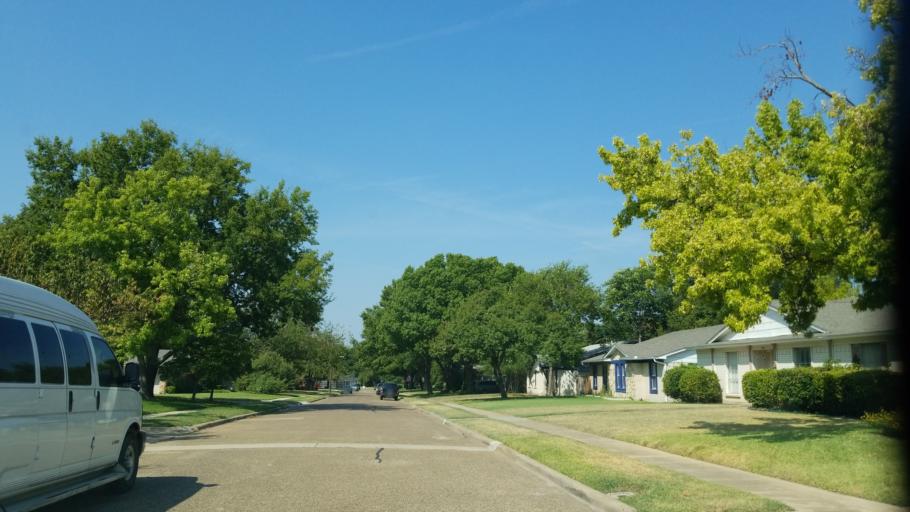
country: US
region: Texas
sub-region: Dallas County
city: Richardson
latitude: 32.9690
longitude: -96.7437
